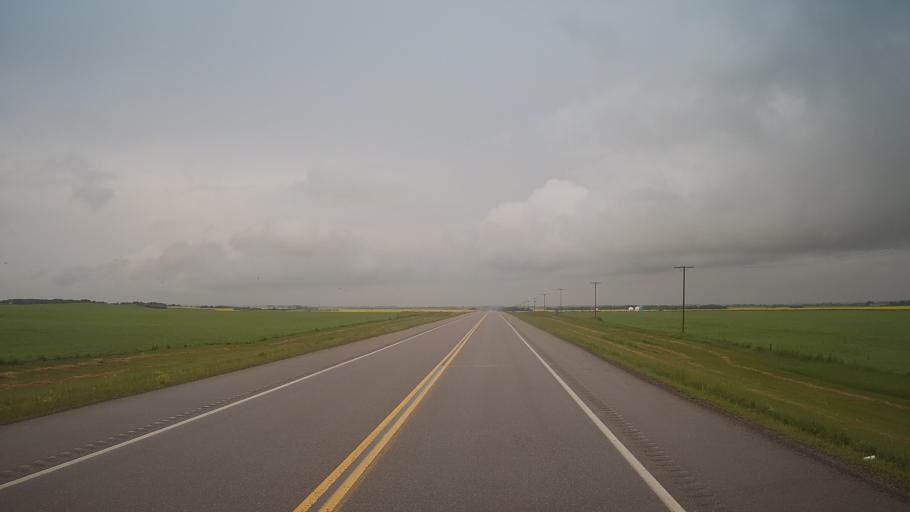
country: CA
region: Saskatchewan
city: Wilkie
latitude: 52.4172
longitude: -108.8873
